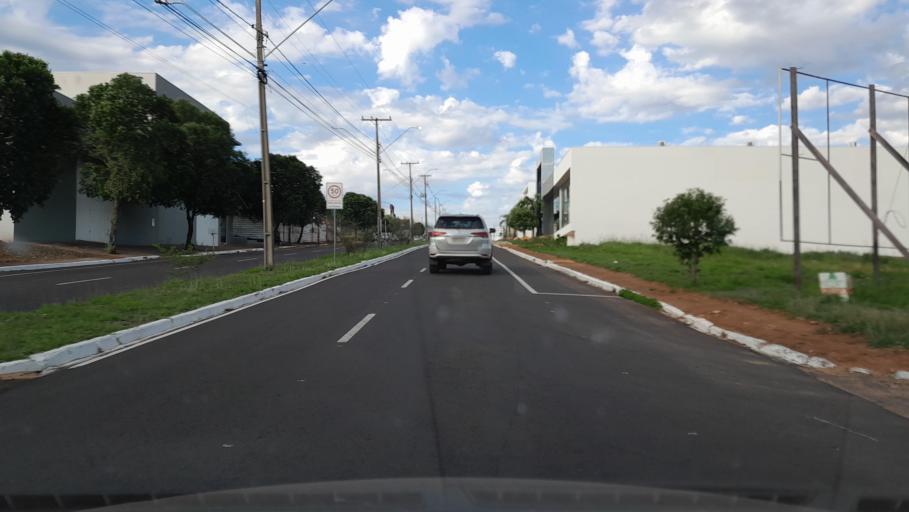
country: BR
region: Parana
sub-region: Umuarama
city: Umuarama
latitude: -23.7533
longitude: -53.2766
